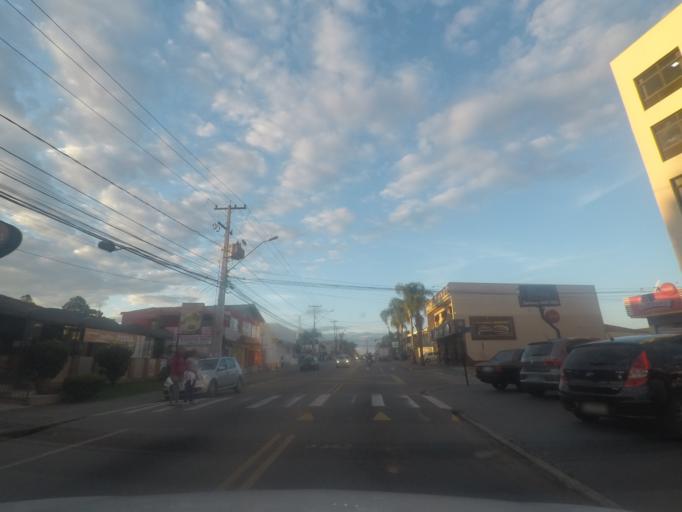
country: BR
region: Parana
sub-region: Pinhais
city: Pinhais
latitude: -25.4407
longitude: -49.1874
